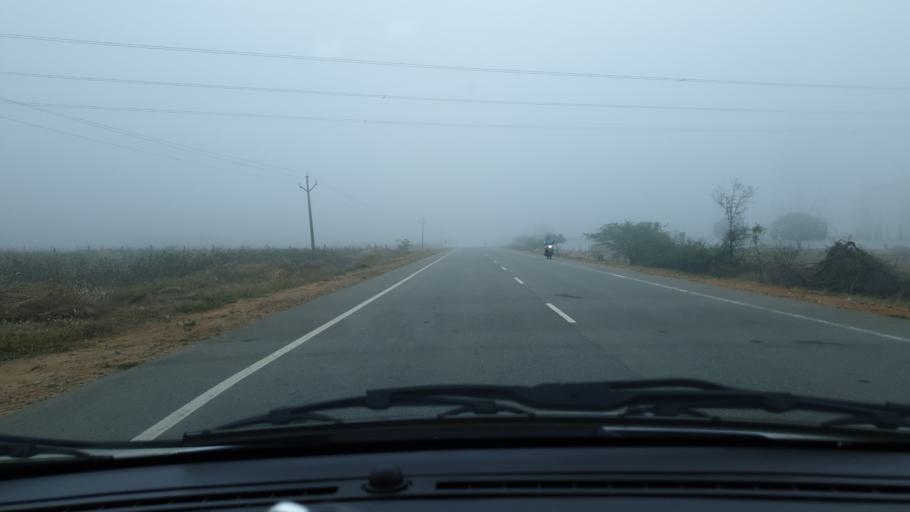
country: IN
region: Telangana
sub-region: Nalgonda
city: Devarkonda
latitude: 16.6185
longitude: 78.6732
